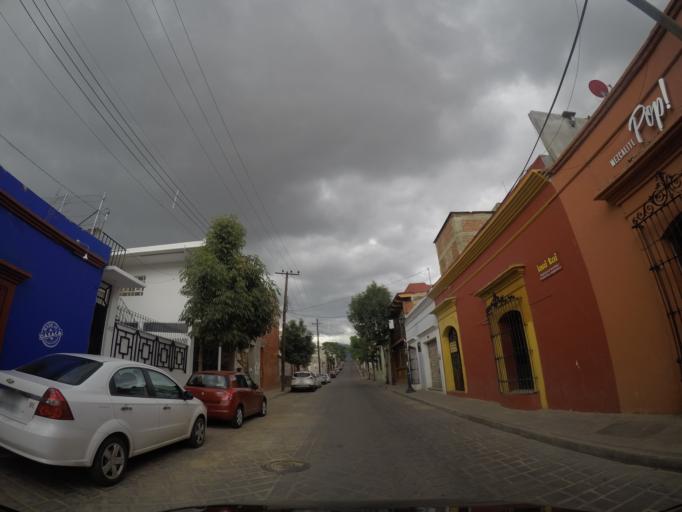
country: MX
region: Oaxaca
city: Oaxaca de Juarez
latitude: 17.0655
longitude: -96.7259
